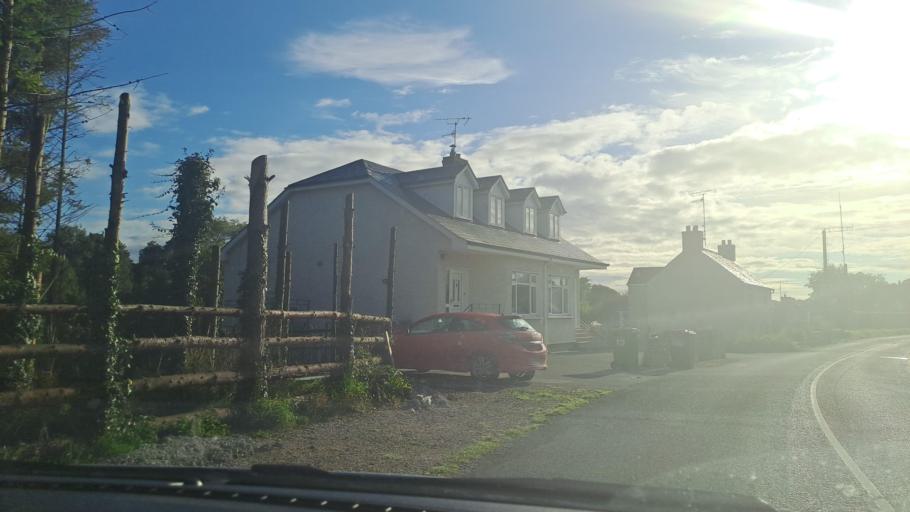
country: IE
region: Ulster
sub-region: County Monaghan
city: Carrickmacross
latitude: 53.9787
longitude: -6.7316
